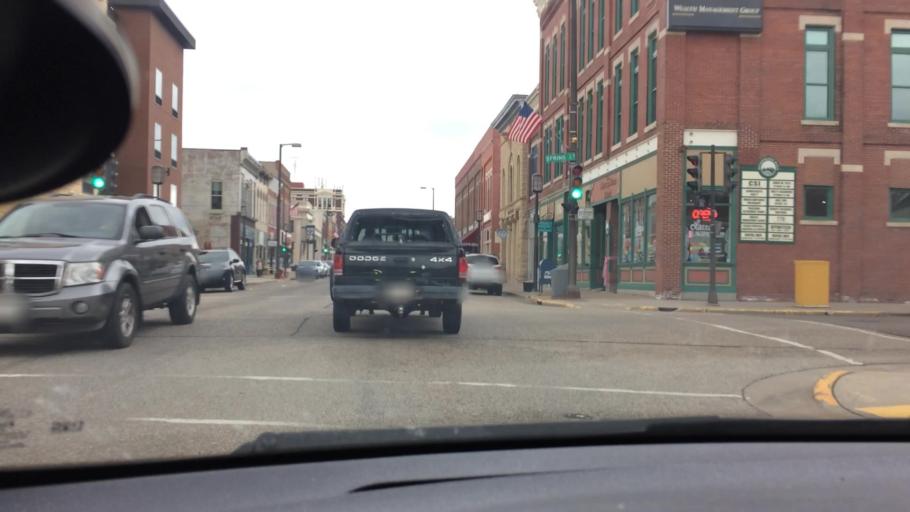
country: US
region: Wisconsin
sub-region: Chippewa County
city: Chippewa Falls
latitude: 44.9356
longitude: -91.3914
